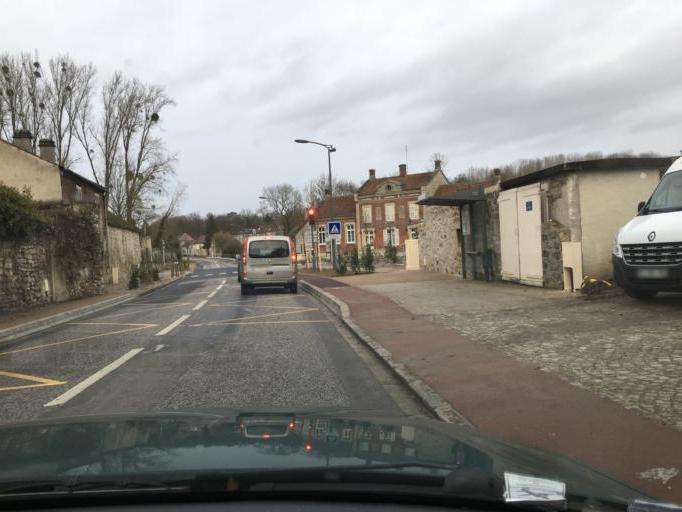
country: FR
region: Picardie
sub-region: Departement de l'Oise
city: Thiers-sur-Theve
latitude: 49.1542
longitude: 2.5497
